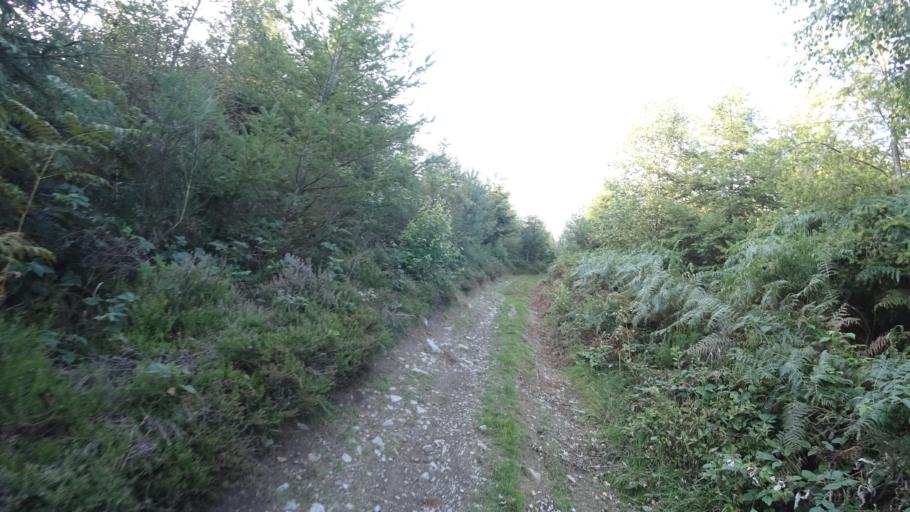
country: BE
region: Wallonia
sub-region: Province du Luxembourg
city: Neufchateau
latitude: 49.8763
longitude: 5.3768
